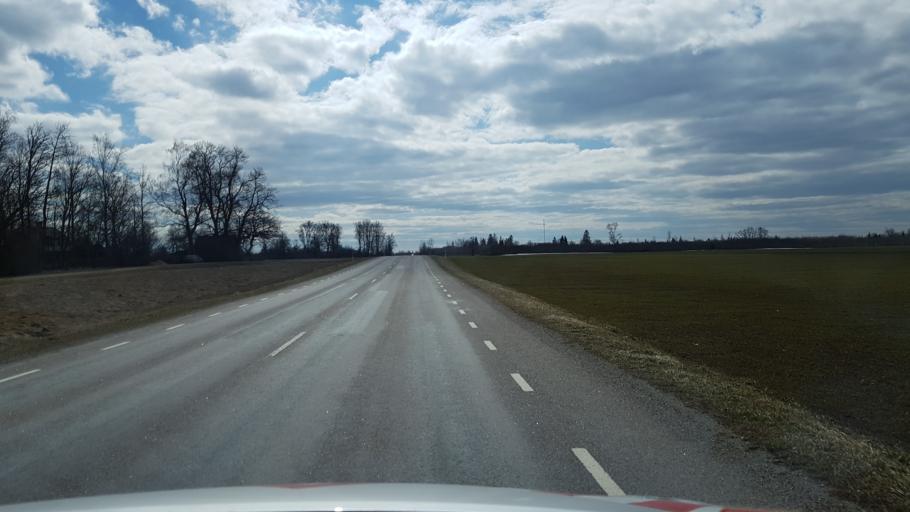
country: EE
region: Laeaene-Virumaa
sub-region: Vaeike-Maarja vald
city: Vaike-Maarja
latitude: 59.1534
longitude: 26.2636
